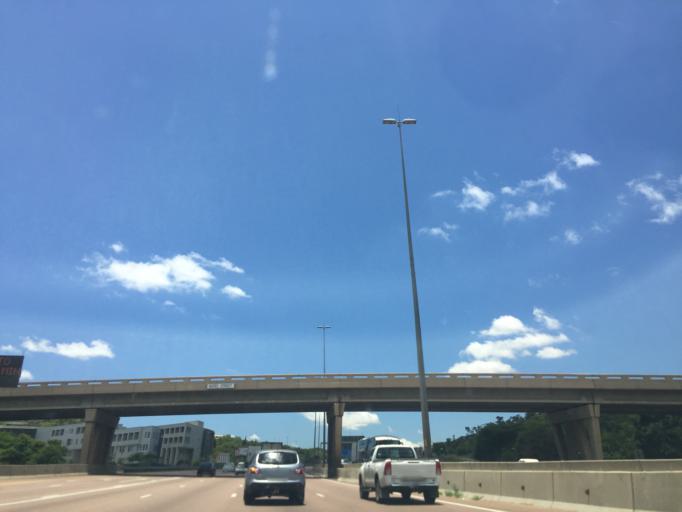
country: ZA
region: Gauteng
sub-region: City of Tshwane Metropolitan Municipality
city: Pretoria
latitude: -25.7484
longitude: 28.2711
